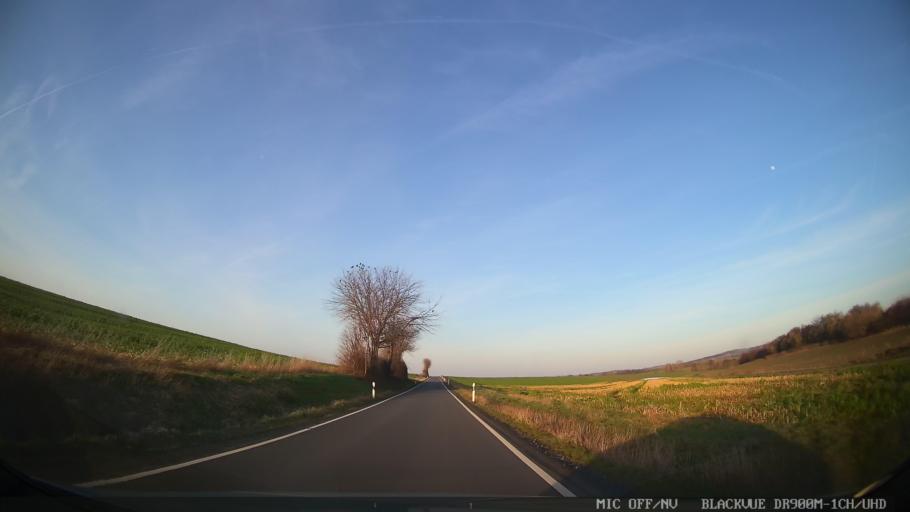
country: DE
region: Hesse
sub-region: Regierungsbezirk Darmstadt
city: Gross-Zimmern
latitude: 49.8565
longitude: 8.8761
